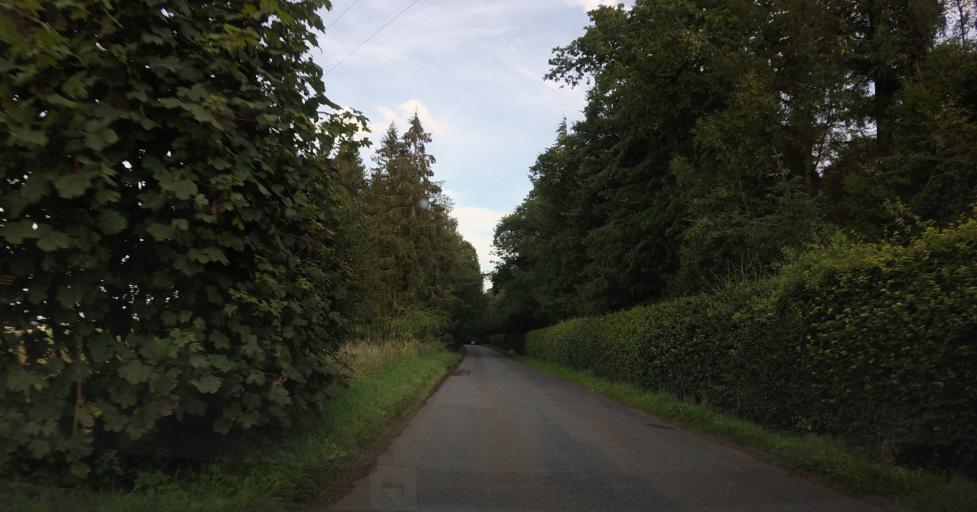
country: GB
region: Scotland
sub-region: Perth and Kinross
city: Auchterarder
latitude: 56.3073
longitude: -3.7332
